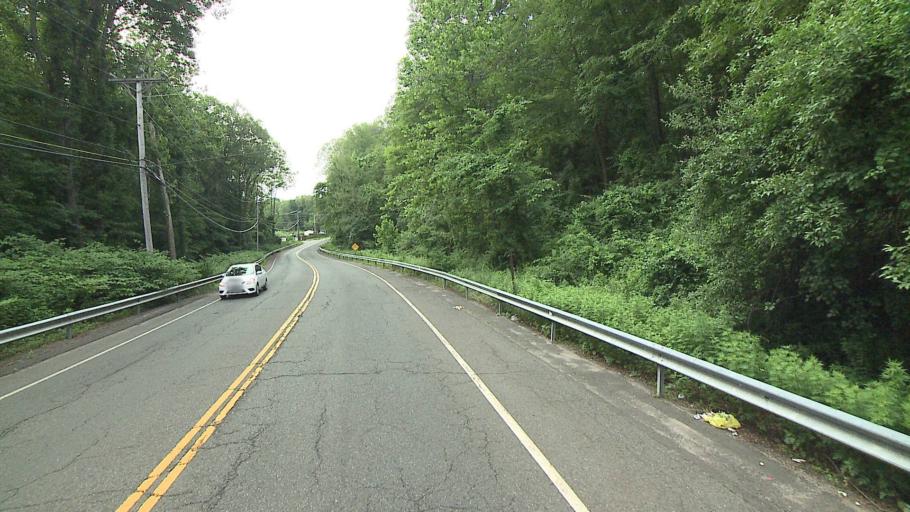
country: US
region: Connecticut
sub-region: New Haven County
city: Southbury
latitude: 41.4721
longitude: -73.2068
